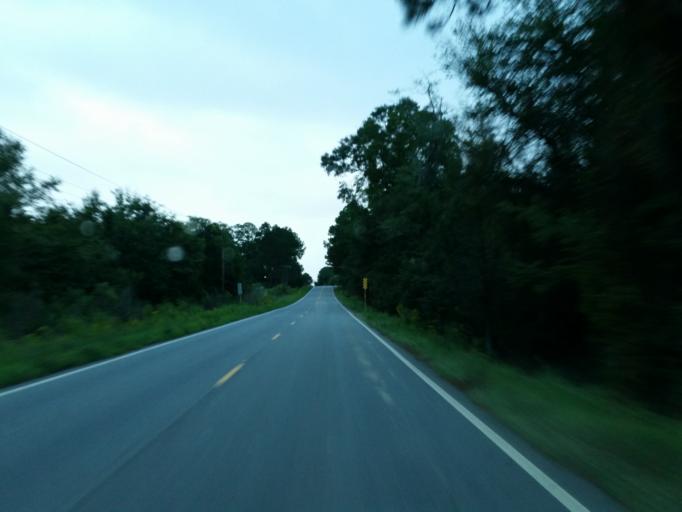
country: US
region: Georgia
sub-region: Crisp County
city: Cordele
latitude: 31.8862
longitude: -83.7556
